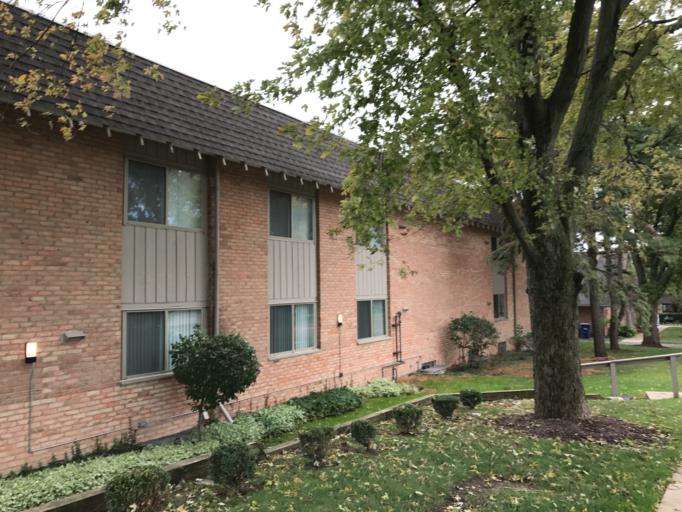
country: US
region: Michigan
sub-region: Washtenaw County
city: Ann Arbor
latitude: 42.2515
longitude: -83.7237
